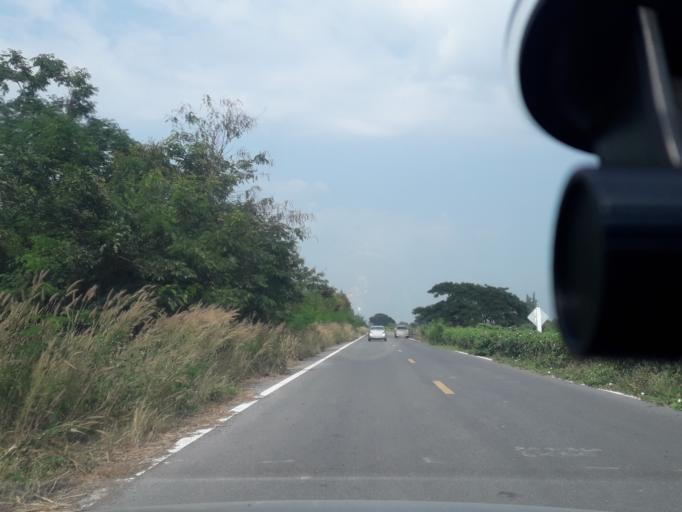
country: TH
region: Sara Buri
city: Nong Khae
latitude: 14.2606
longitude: 100.8912
